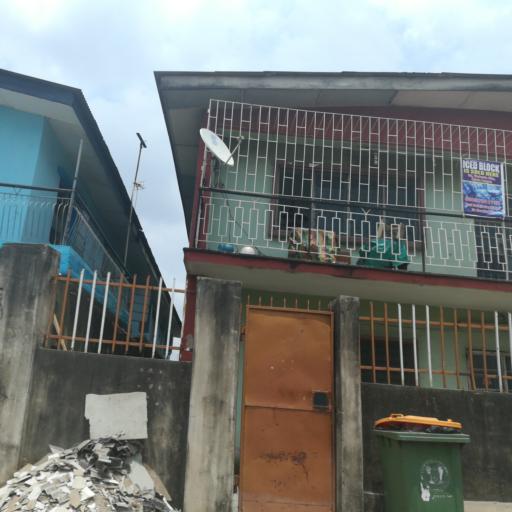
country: NG
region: Lagos
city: Ojota
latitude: 6.5817
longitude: 3.3817
